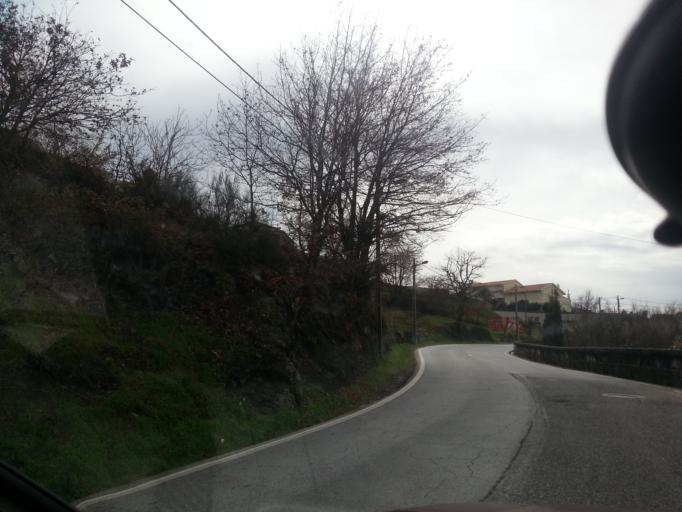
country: PT
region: Guarda
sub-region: Seia
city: Seia
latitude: 40.3965
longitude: -7.7129
